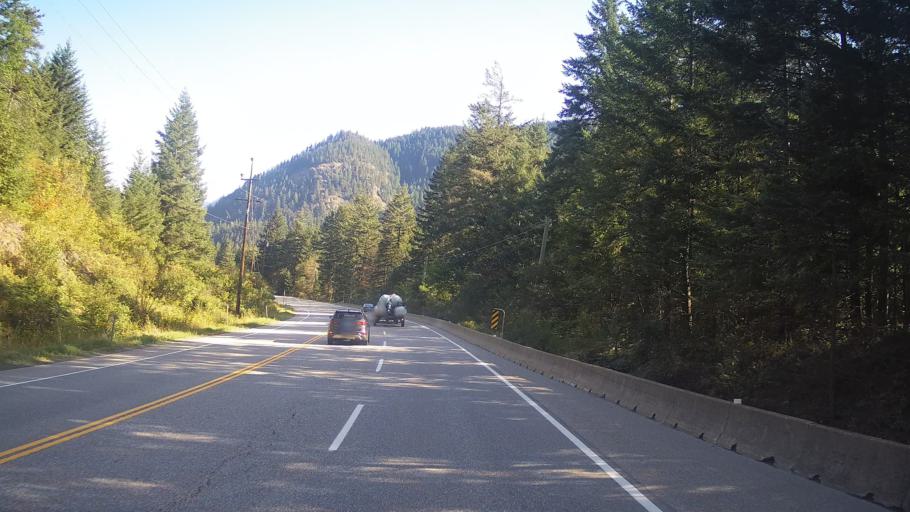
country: CA
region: British Columbia
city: Hope
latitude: 49.6533
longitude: -121.4061
